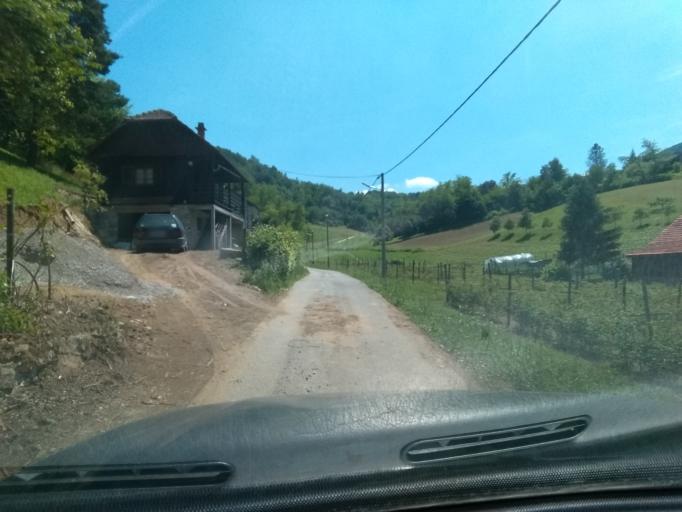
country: SI
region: Bistrica ob Sotli
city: Bistrica ob Sotli
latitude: 46.0727
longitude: 15.7446
